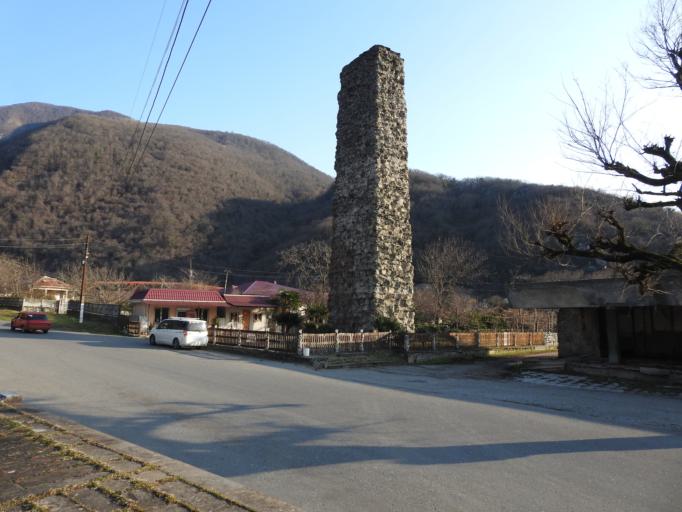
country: GE
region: Abkhazia
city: Bich'vinta
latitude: 43.2395
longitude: 40.3970
